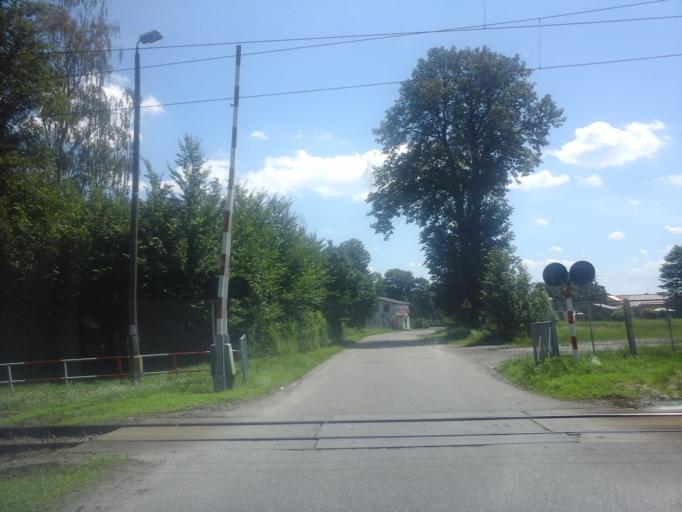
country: PL
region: West Pomeranian Voivodeship
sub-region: Powiat bialogardzki
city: Bialogard
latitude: 54.0950
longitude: 16.0550
